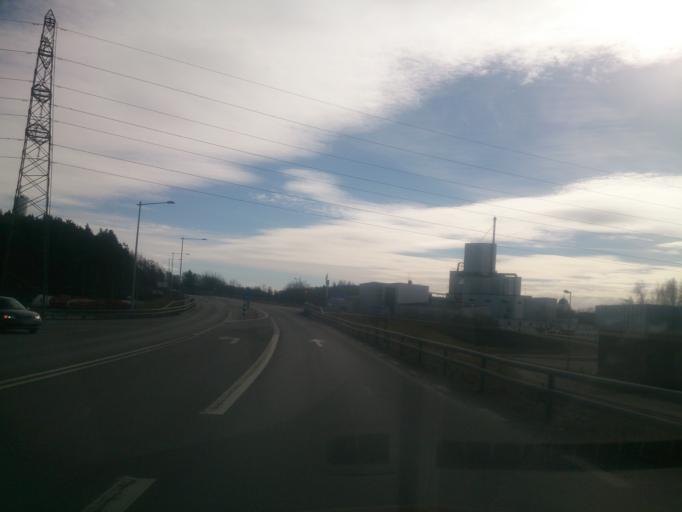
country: SE
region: OEstergoetland
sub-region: Norrkopings Kommun
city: Kimstad
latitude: 58.5462
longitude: 15.9688
